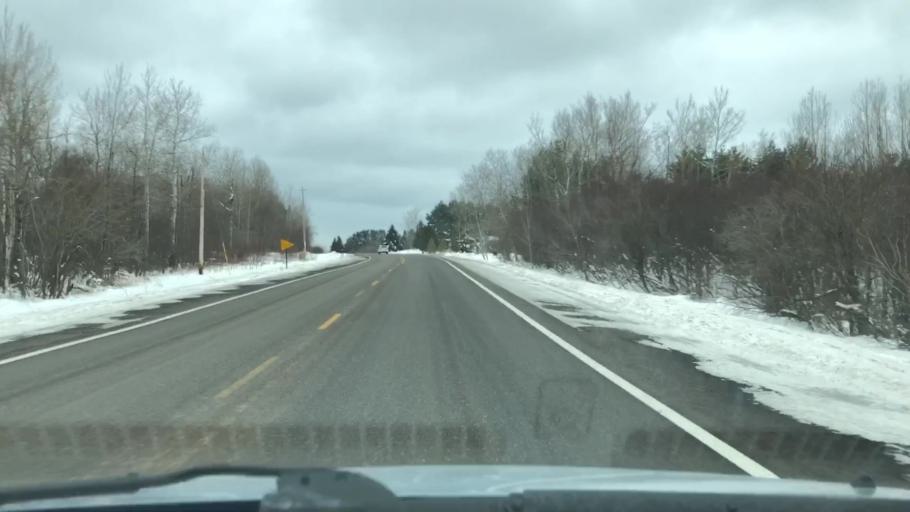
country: US
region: Minnesota
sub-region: Carlton County
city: Esko
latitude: 46.6821
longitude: -92.3688
